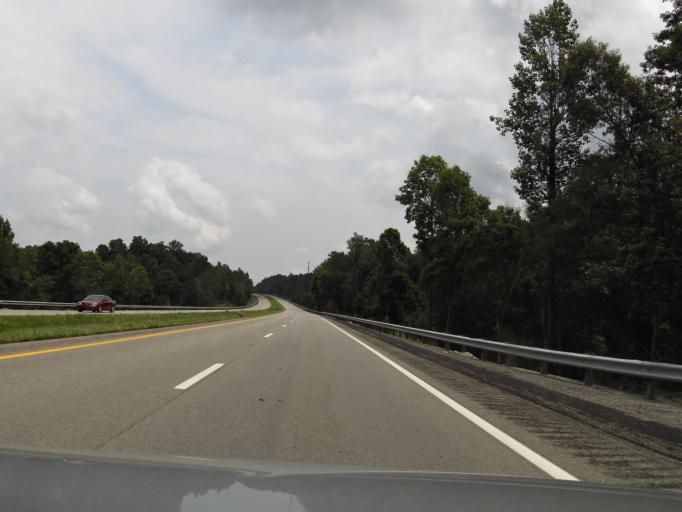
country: US
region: Kentucky
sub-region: Grayson County
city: Leitchfield
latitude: 37.5525
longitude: -86.0925
